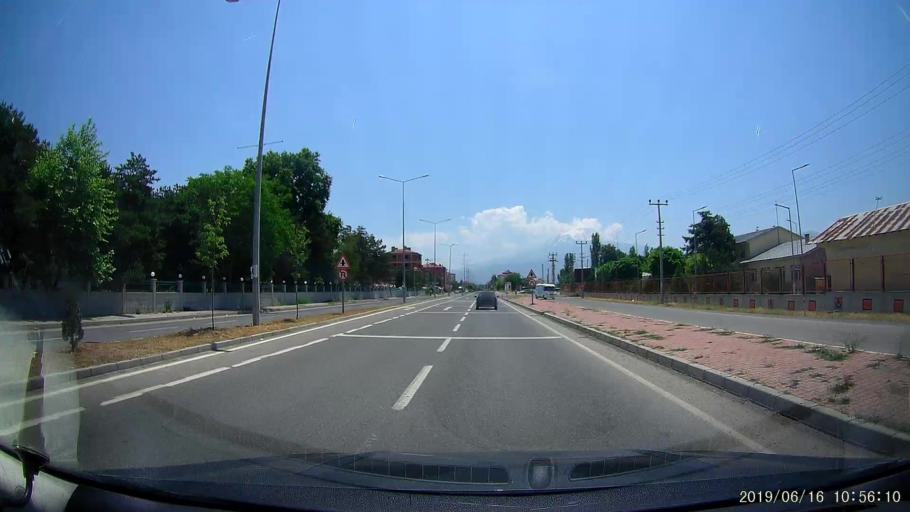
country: TR
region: Igdir
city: Igdir
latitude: 39.9316
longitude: 44.0191
